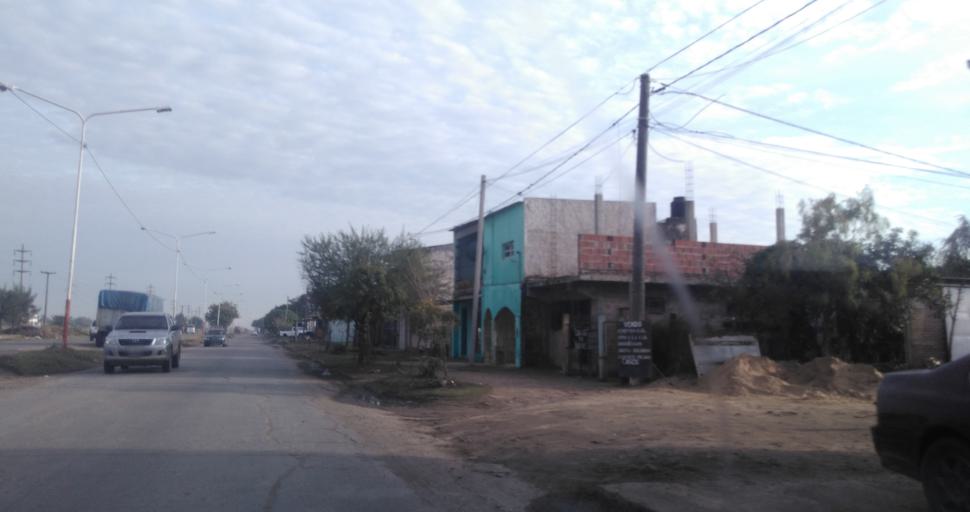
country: AR
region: Chaco
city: Resistencia
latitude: -27.4827
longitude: -58.9940
